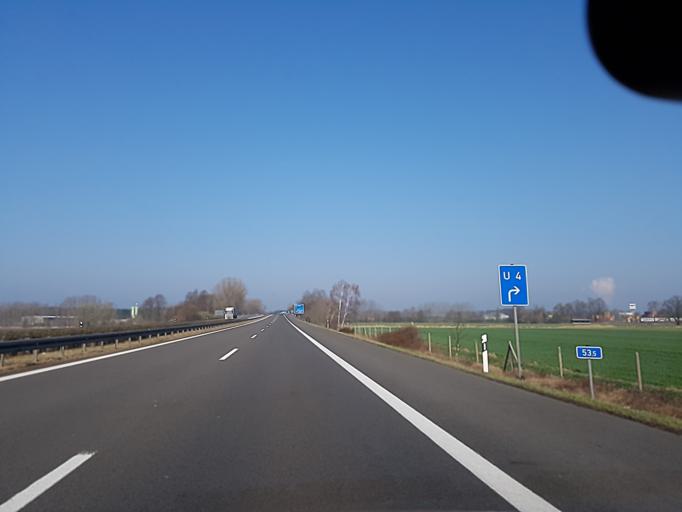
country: DE
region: Brandenburg
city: Forst
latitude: 51.7091
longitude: 14.6226
